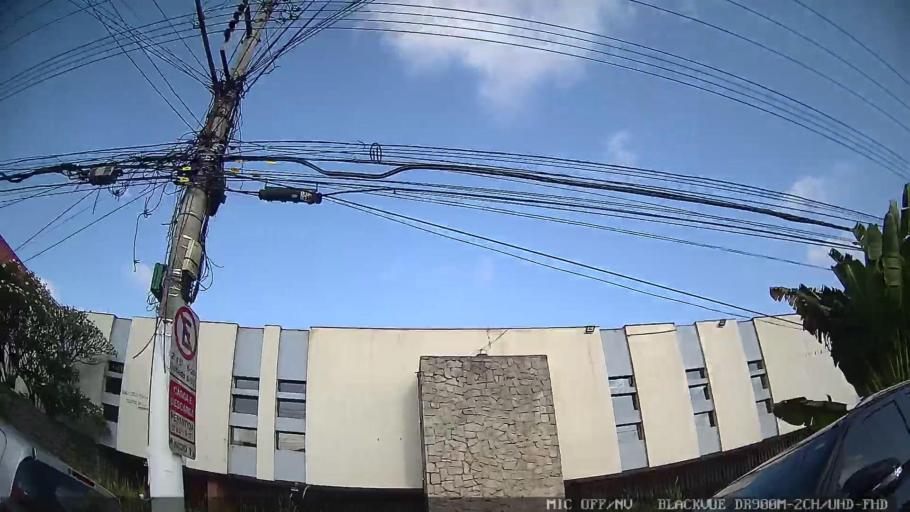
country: BR
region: Sao Paulo
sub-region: Sao Caetano Do Sul
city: Sao Caetano do Sul
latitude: -23.5719
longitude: -46.5406
